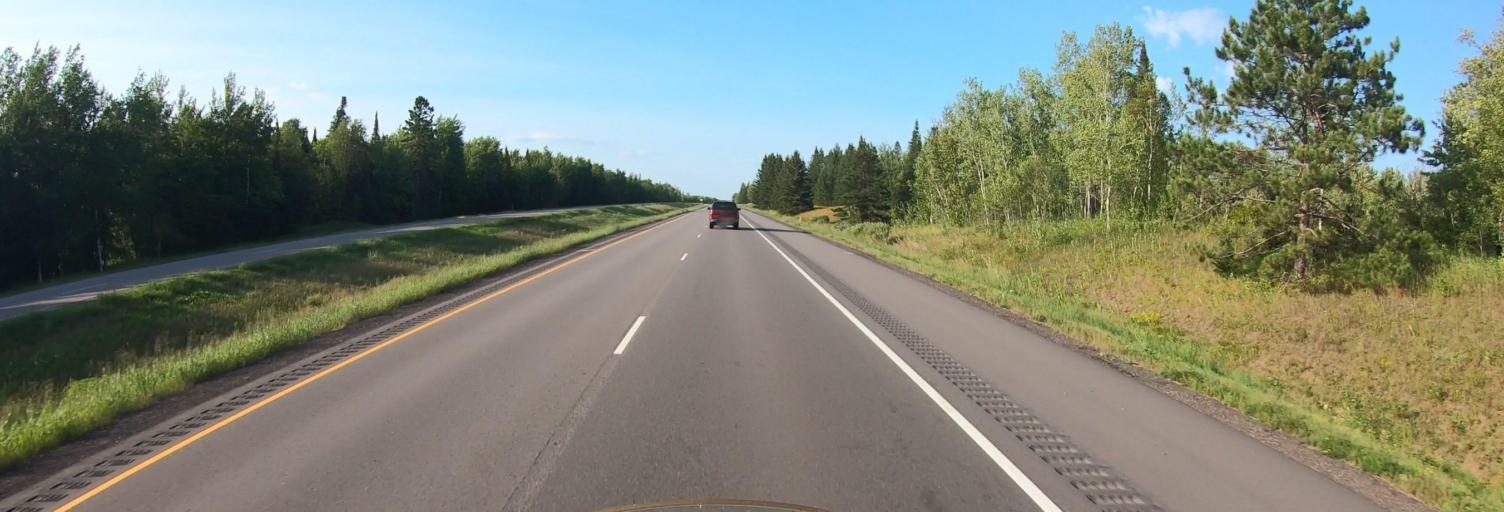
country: US
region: Minnesota
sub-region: Saint Louis County
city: Eveleth
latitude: 47.2590
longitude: -92.4815
